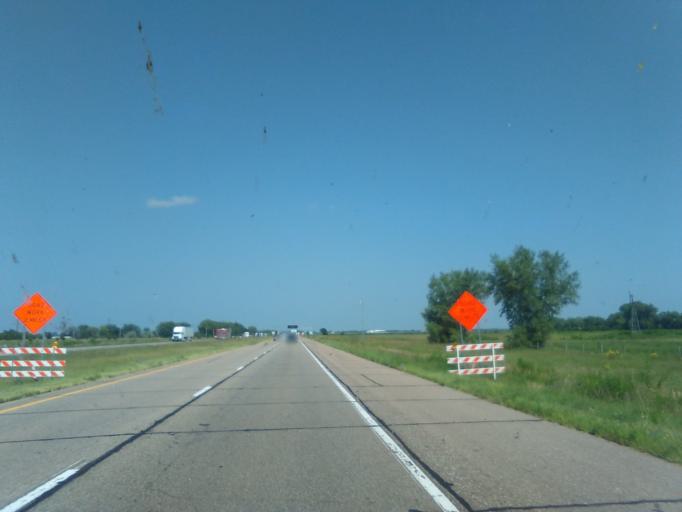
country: US
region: Nebraska
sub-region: Buffalo County
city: Kearney
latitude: 40.6702
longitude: -99.1322
